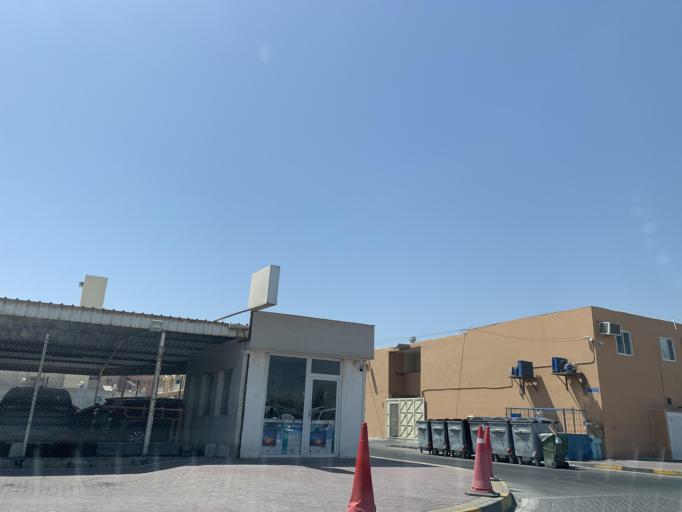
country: BH
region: Muharraq
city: Al Muharraq
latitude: 26.2675
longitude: 50.6162
